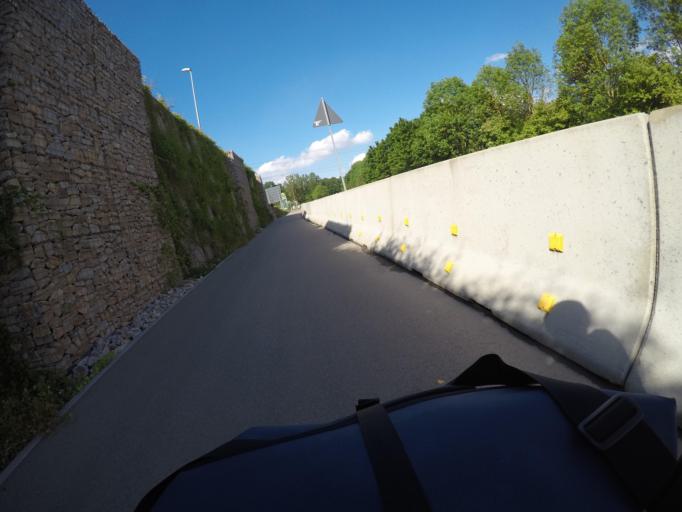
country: DE
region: Baden-Wuerttemberg
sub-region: Regierungsbezirk Stuttgart
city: Ehningen
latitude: 48.6622
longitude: 8.9547
